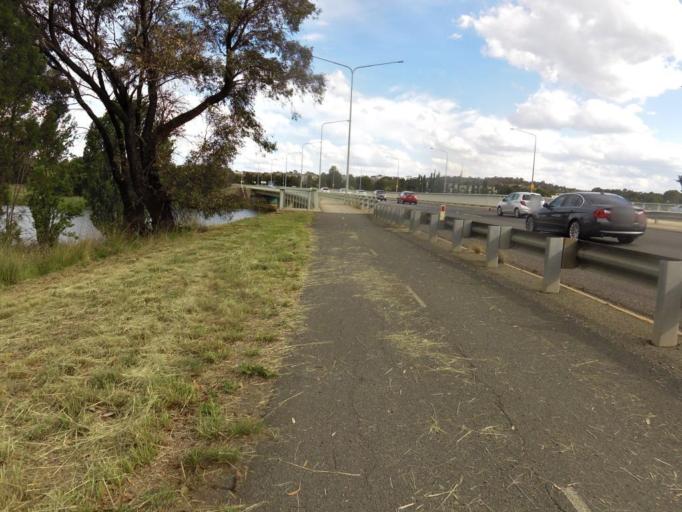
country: AU
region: Australian Capital Territory
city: Belconnen
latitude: -35.2284
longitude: 149.0762
